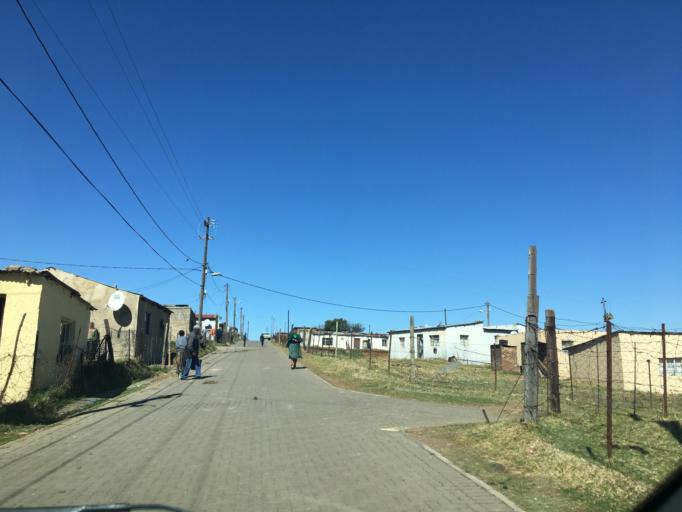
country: ZA
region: Eastern Cape
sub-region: Chris Hani District Municipality
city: Elliot
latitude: -31.3371
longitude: 27.8607
